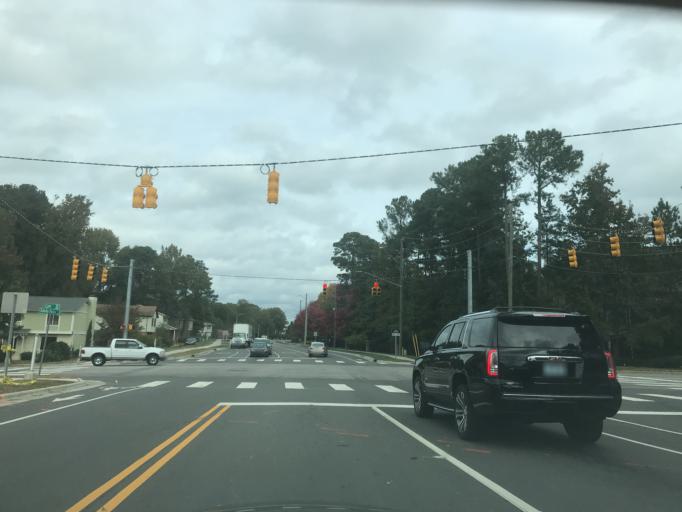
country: US
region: North Carolina
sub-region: Wake County
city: West Raleigh
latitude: 35.8635
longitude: -78.6357
